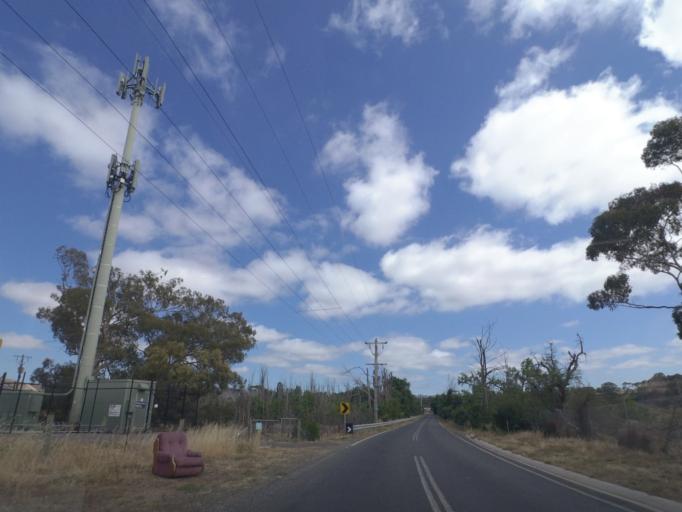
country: AU
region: Victoria
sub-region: Moorabool
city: Bacchus Marsh
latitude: -37.6496
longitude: 144.4499
